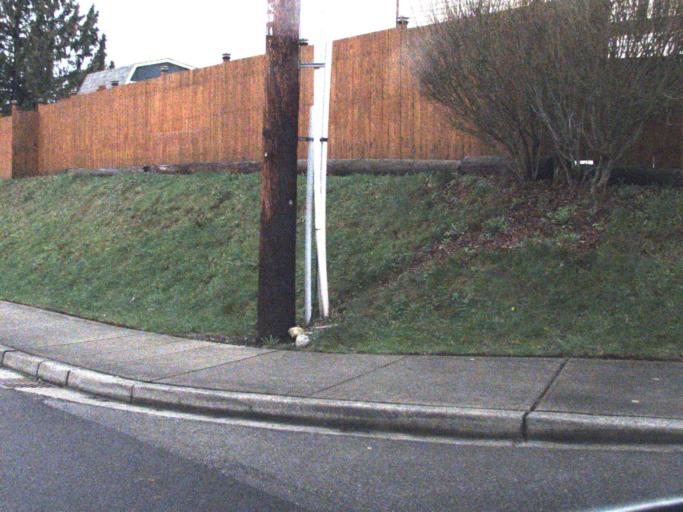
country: US
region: Washington
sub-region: Snohomish County
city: Marysville
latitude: 48.0537
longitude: -122.1337
